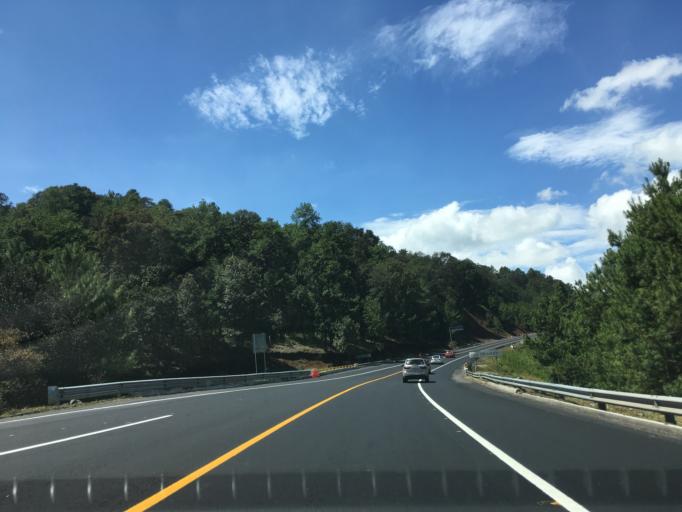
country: MX
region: Michoacan
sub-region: Patzcuaro
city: Santa Maria Huiramangaro (San Juan Tumbio)
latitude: 19.4817
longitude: -101.7280
